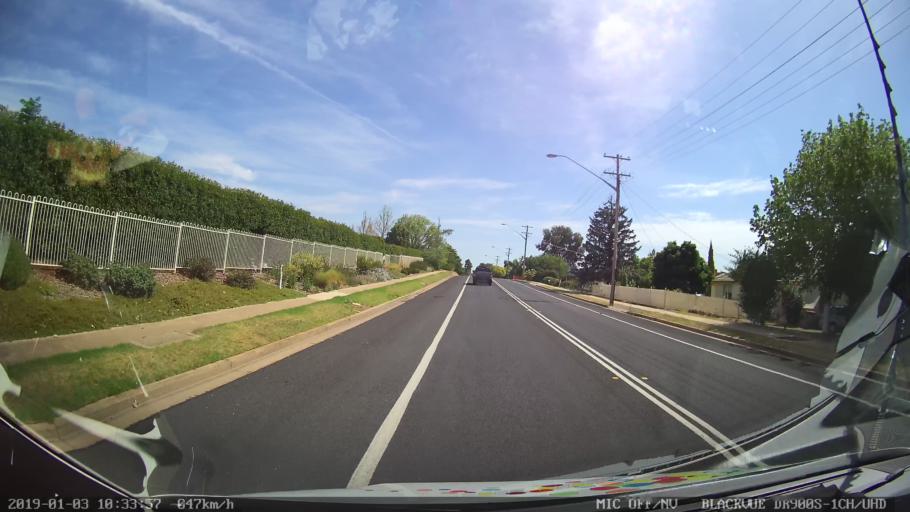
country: AU
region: New South Wales
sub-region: Young
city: Young
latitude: -34.3248
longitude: 148.2903
